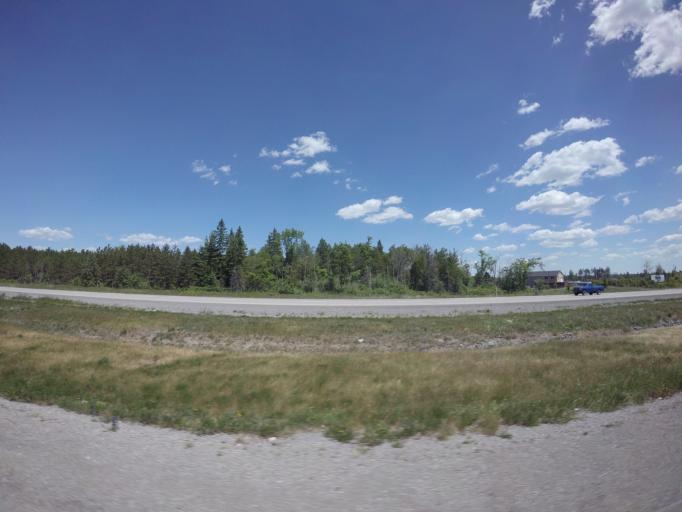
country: CA
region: Ontario
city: Bells Corners
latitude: 45.2573
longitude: -75.9716
